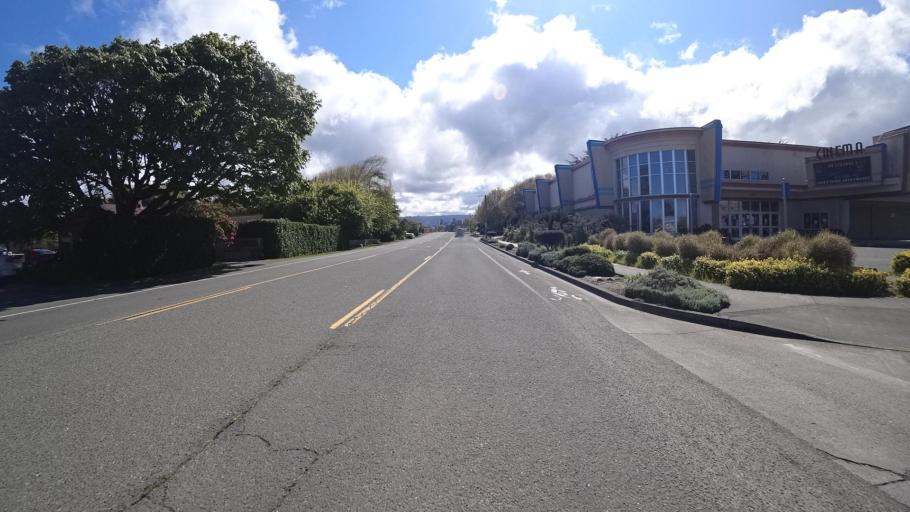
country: US
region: California
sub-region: Humboldt County
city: McKinleyville
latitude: 40.9342
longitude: -124.1046
